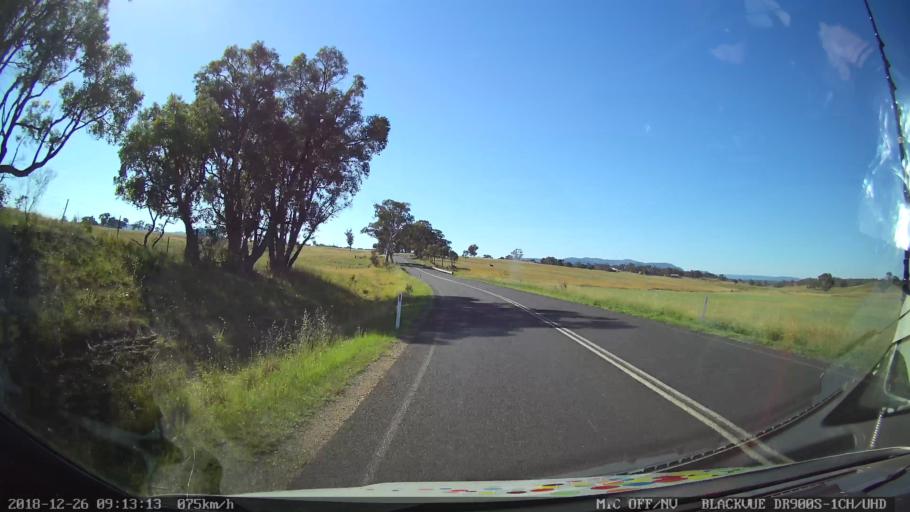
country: AU
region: New South Wales
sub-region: Mid-Western Regional
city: Kandos
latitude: -32.7656
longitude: 149.9776
